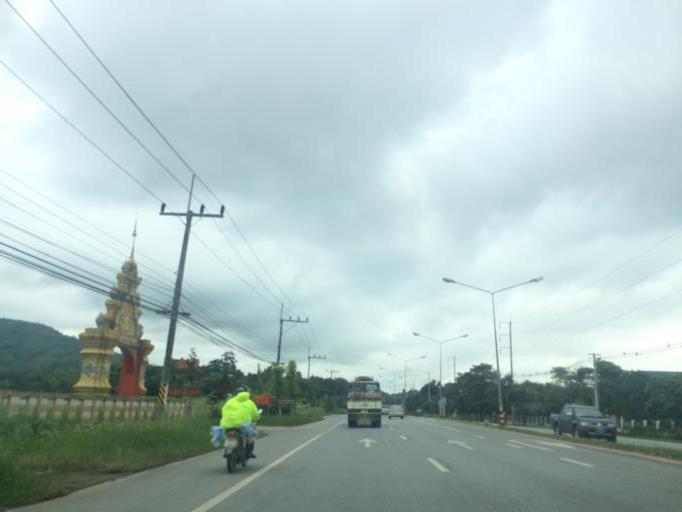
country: TH
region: Chiang Rai
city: Mae Chan
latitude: 20.0993
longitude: 99.8742
